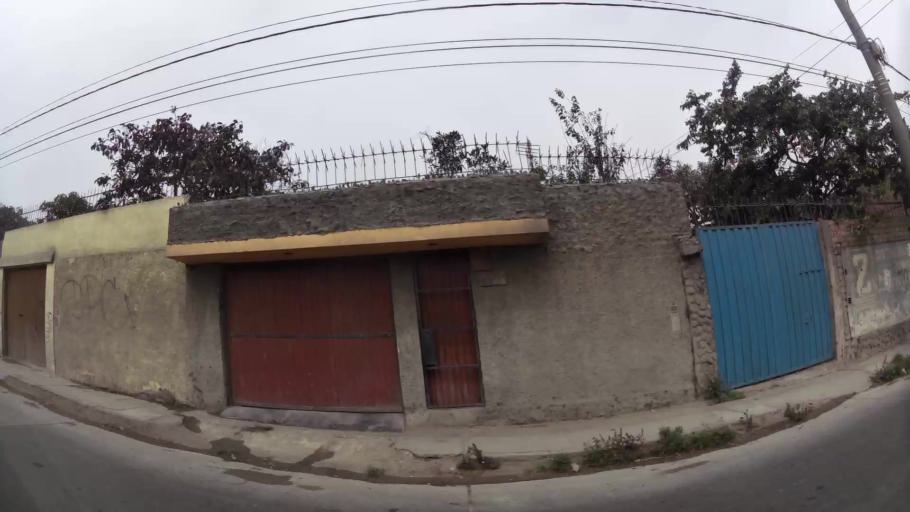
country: PE
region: Lima
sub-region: Lima
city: Chaclacayo
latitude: -11.9714
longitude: -76.7545
